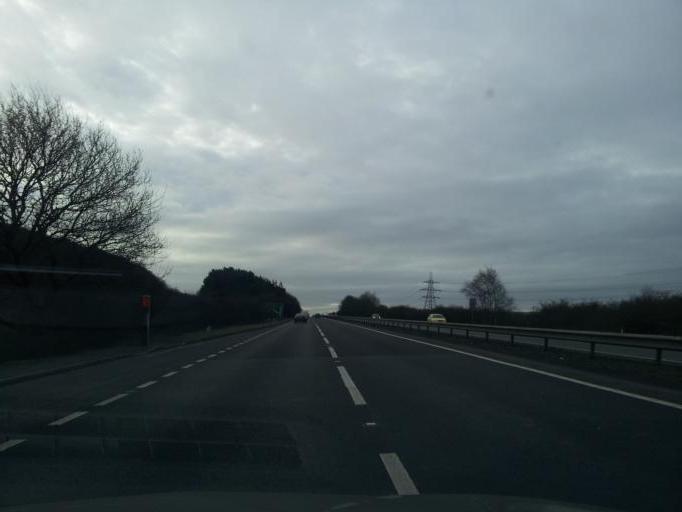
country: GB
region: England
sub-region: Lincolnshire
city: Barrowby
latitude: 52.9273
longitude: -0.6829
